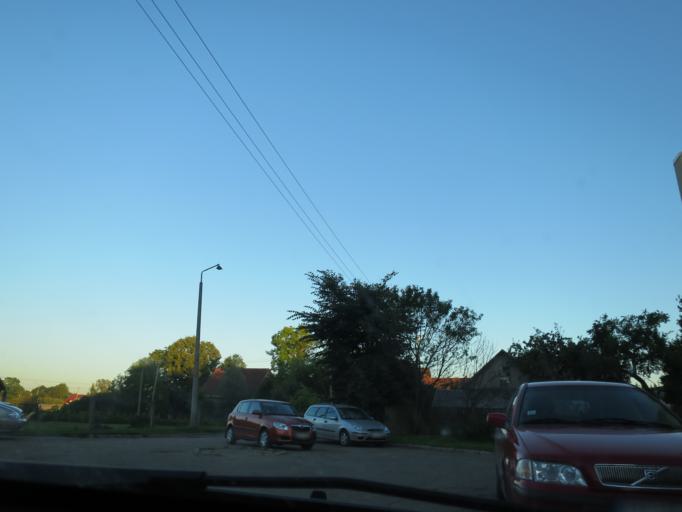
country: LV
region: Sigulda
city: Sigulda
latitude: 57.1448
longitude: 24.8467
